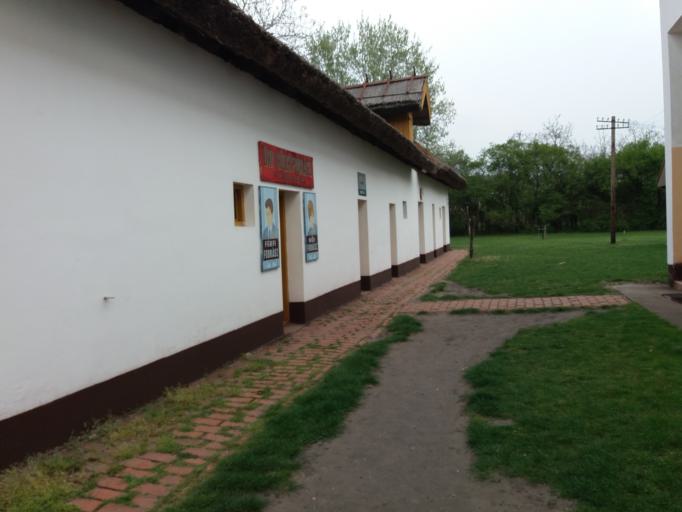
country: HU
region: Csongrad
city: Opusztaszer
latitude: 46.4865
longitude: 20.0985
